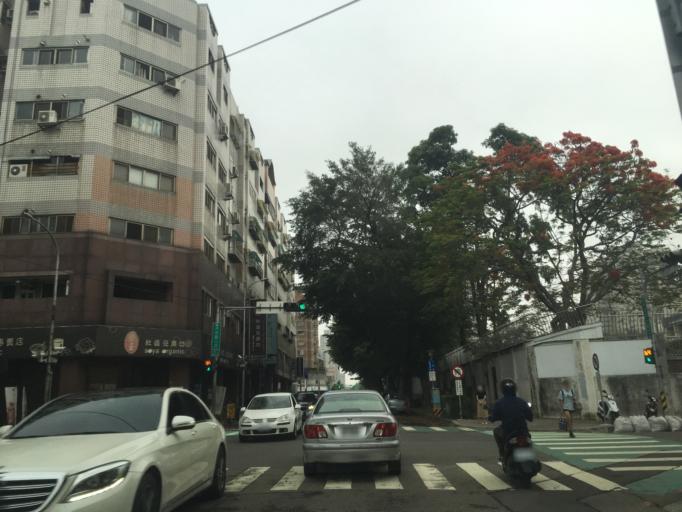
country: TW
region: Taiwan
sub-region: Taichung City
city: Taichung
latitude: 24.1746
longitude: 120.6836
